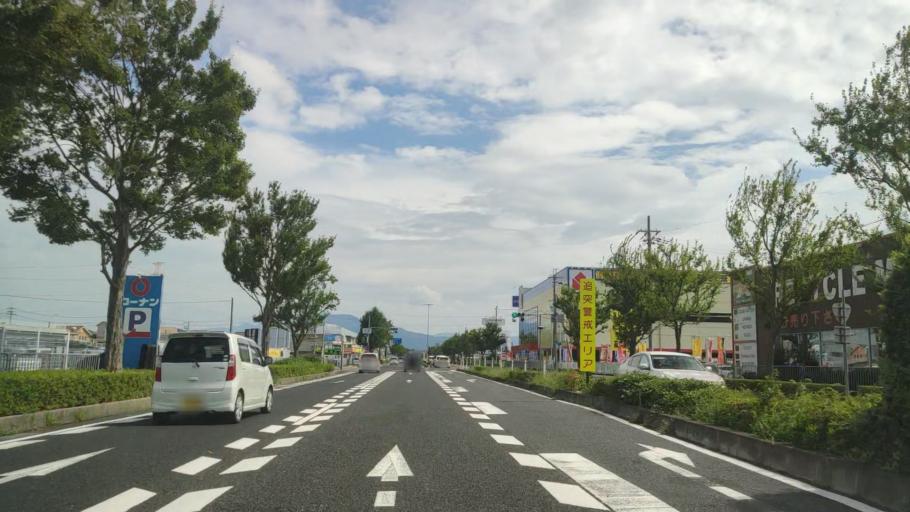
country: JP
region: Wakayama
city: Iwade
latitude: 34.2623
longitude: 135.2920
